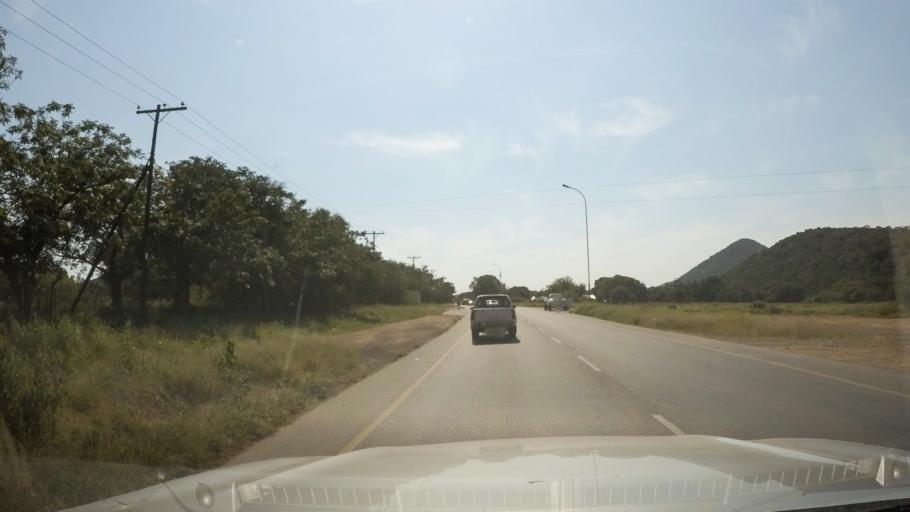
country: BW
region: South East
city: Lobatse
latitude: -25.2217
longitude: 25.6792
